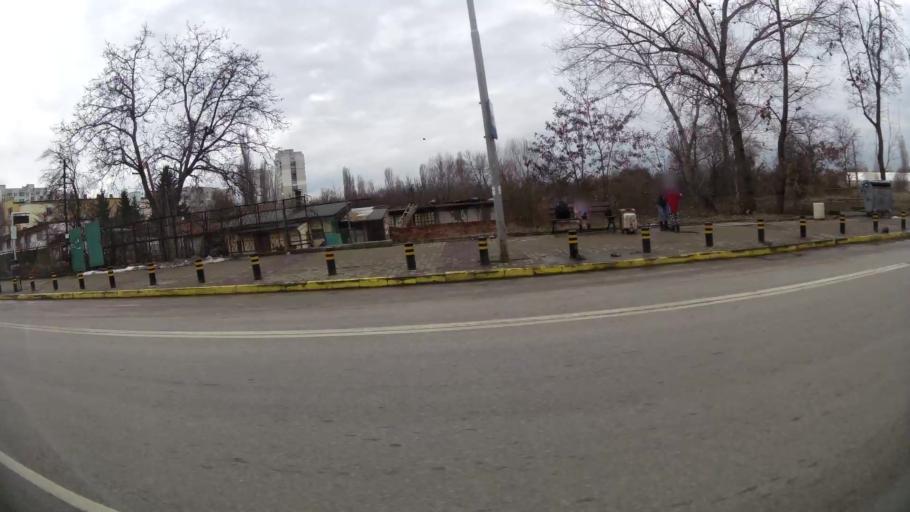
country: BG
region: Sofia-Capital
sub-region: Stolichna Obshtina
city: Sofia
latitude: 42.7399
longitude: 23.2878
